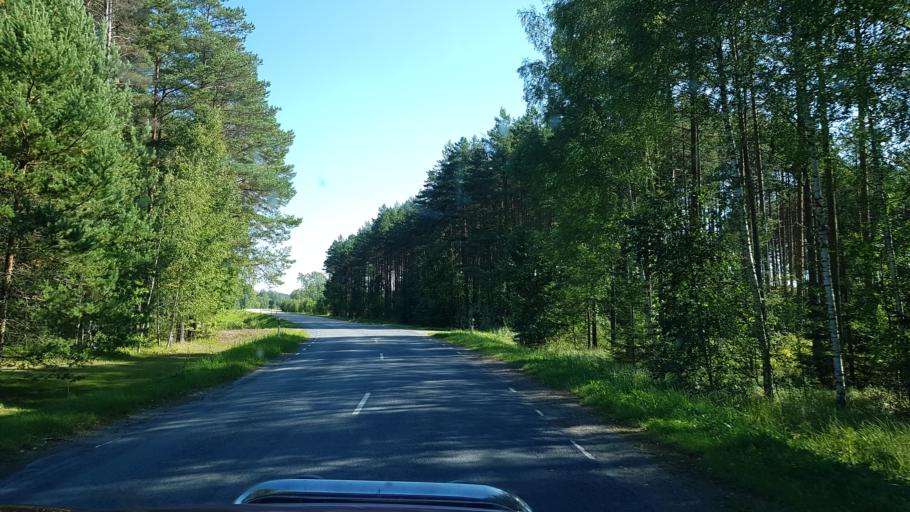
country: EE
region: Polvamaa
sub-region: Polva linn
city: Polva
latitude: 58.2674
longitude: 27.1386
